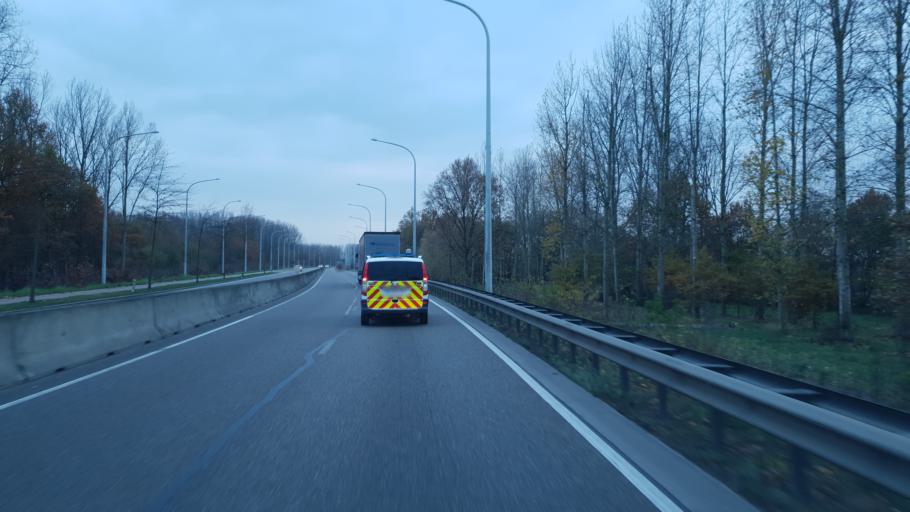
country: BE
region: Flanders
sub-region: Provincie Limburg
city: Diepenbeek
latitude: 50.9165
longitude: 5.4386
